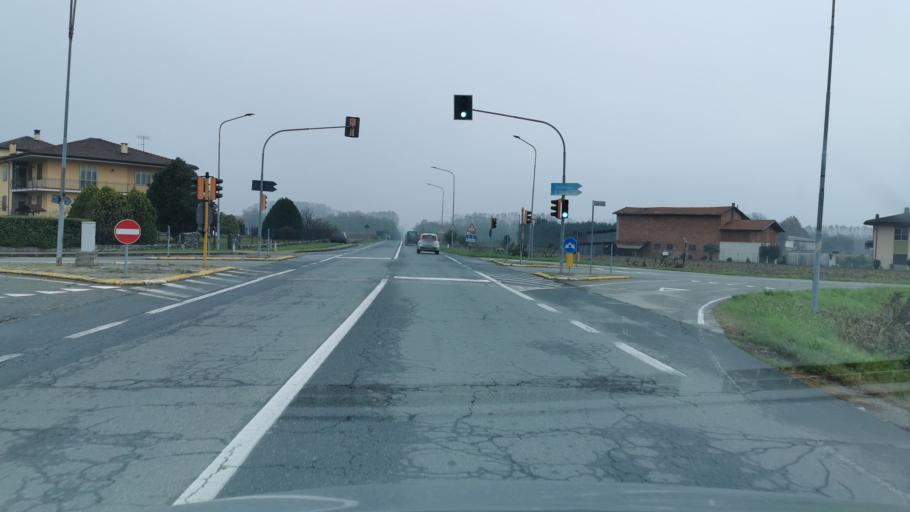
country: IT
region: Piedmont
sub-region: Provincia di Torino
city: Strambino
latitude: 45.3797
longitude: 7.8954
